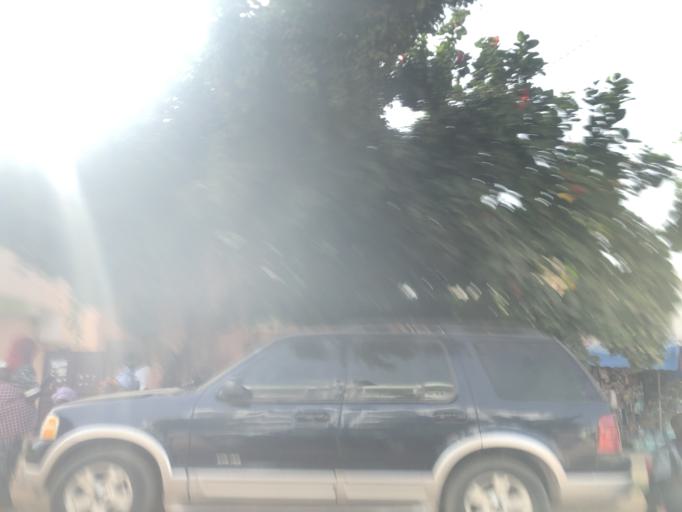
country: SN
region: Dakar
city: Mermoz Boabab
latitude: 14.7322
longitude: -17.4932
